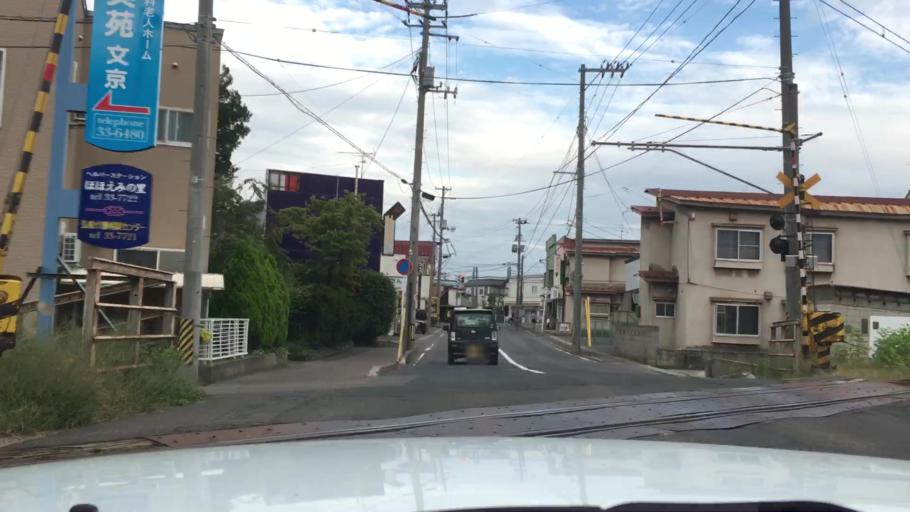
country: JP
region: Aomori
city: Hirosaki
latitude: 40.5854
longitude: 140.4700
